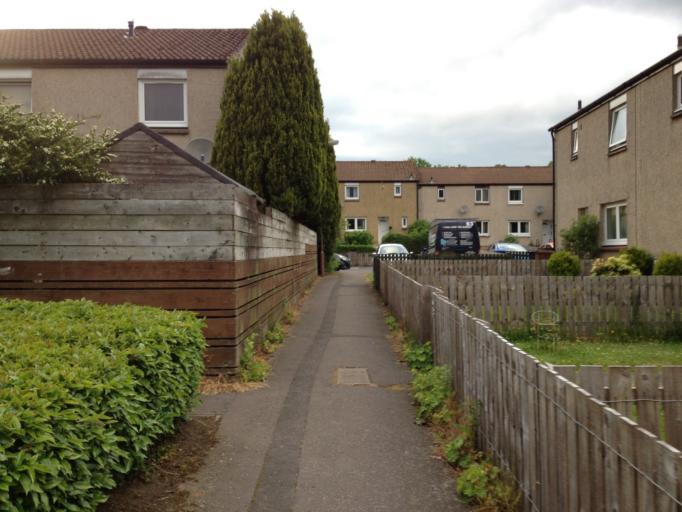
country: GB
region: Scotland
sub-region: West Lothian
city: Livingston
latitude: 55.8947
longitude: -3.5329
